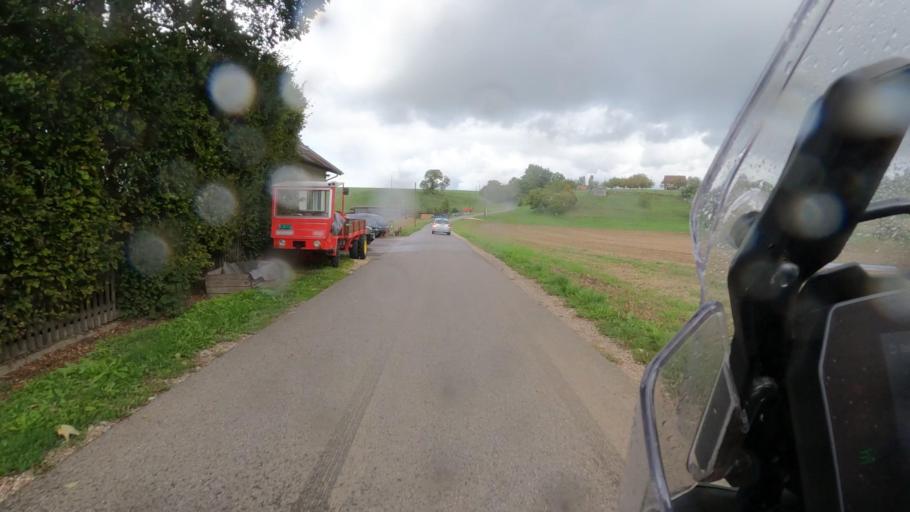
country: CH
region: Schaffhausen
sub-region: Bezirk Unterklettgau
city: Wilchingen
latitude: 47.6616
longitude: 8.4662
